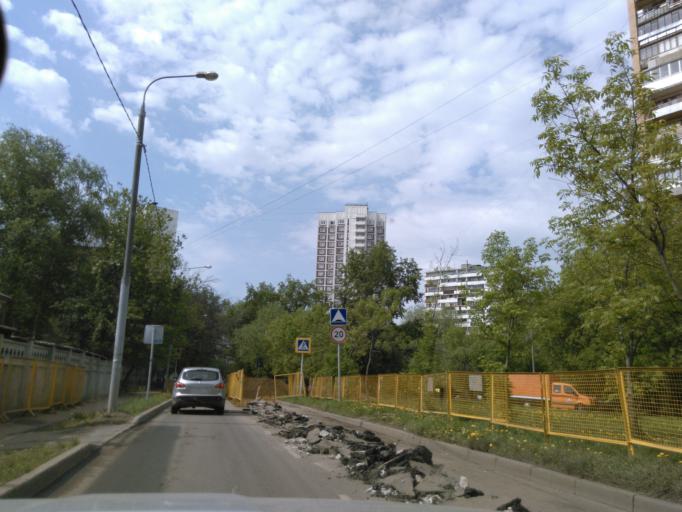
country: RU
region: Moscow
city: Novokhovrino
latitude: 55.8617
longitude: 37.5156
